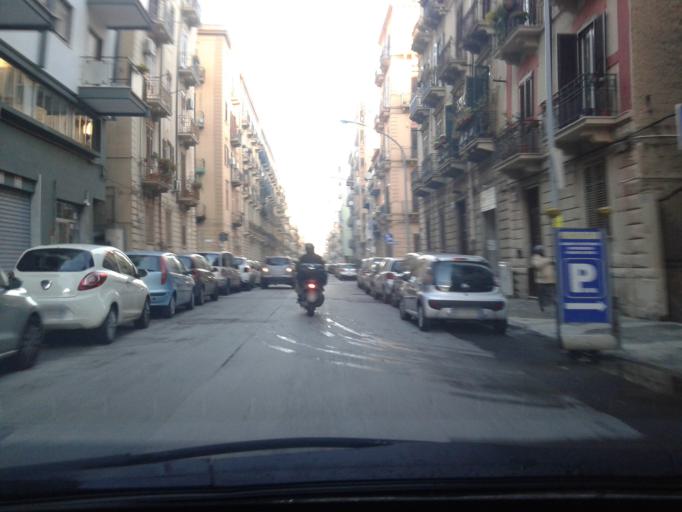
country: IT
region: Sicily
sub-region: Palermo
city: Palermo
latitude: 38.1187
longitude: 13.3460
